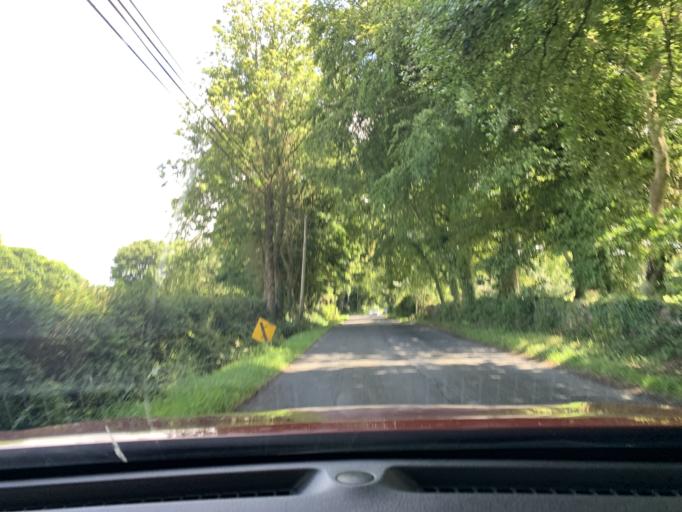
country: IE
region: Connaught
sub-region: County Leitrim
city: Carrick-on-Shannon
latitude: 53.8484
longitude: -8.1780
